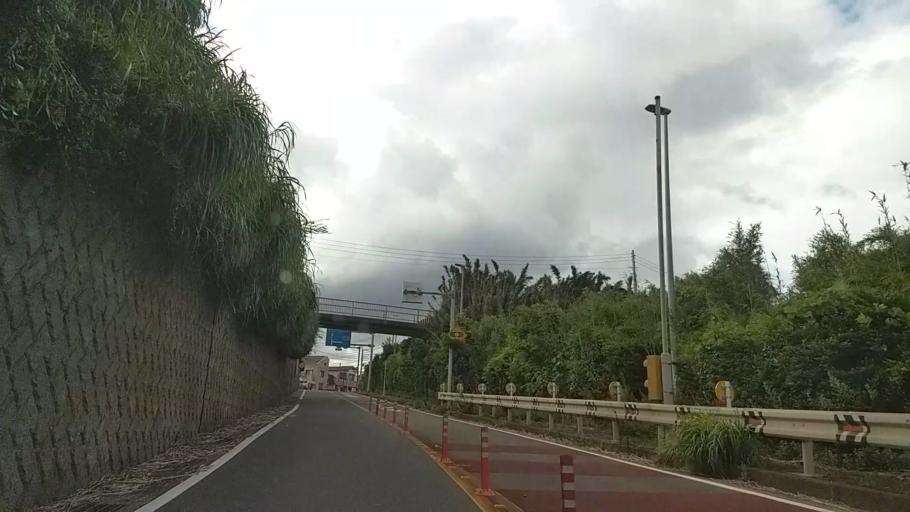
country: JP
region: Kanagawa
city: Miura
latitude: 35.1455
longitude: 139.6709
